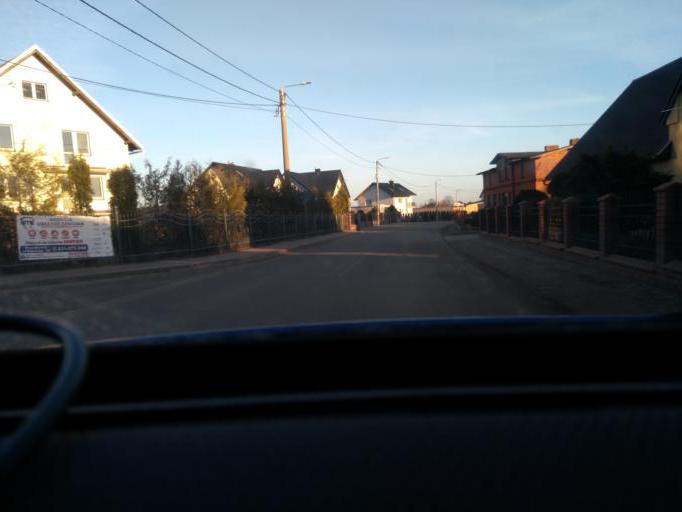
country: PL
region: Pomeranian Voivodeship
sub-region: Powiat kartuski
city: Przodkowo
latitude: 54.4140
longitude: 18.3187
